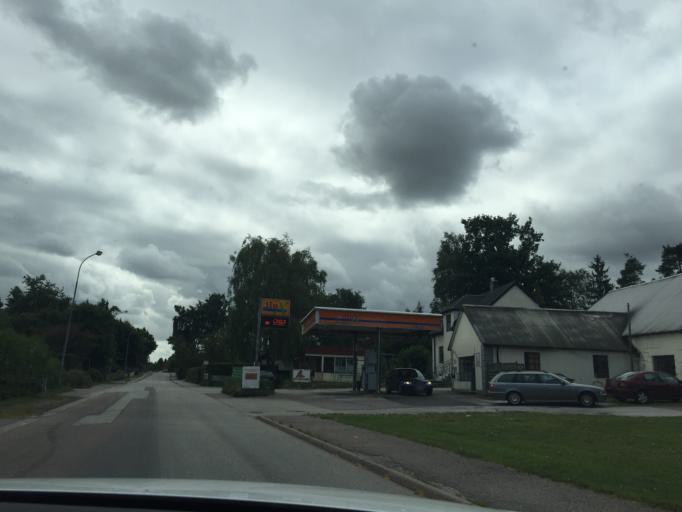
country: SE
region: Skane
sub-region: Sjobo Kommun
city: Blentarp
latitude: 55.5911
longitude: 13.5992
